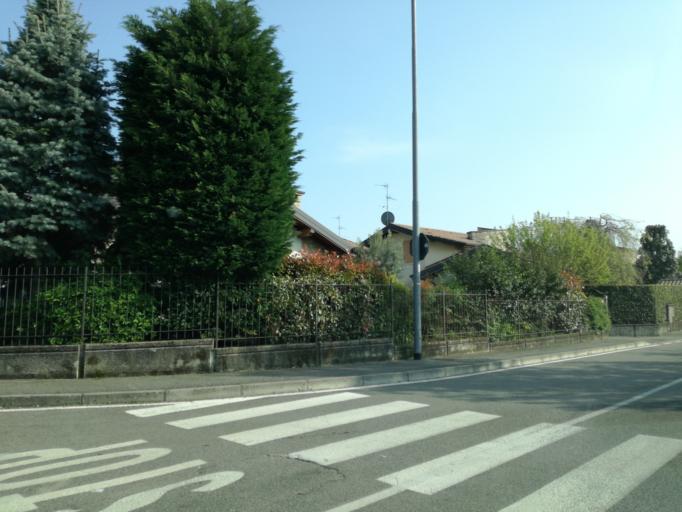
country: IT
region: Lombardy
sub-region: Provincia di Lecco
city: Verderio Inferiore
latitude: 45.6658
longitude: 9.4321
